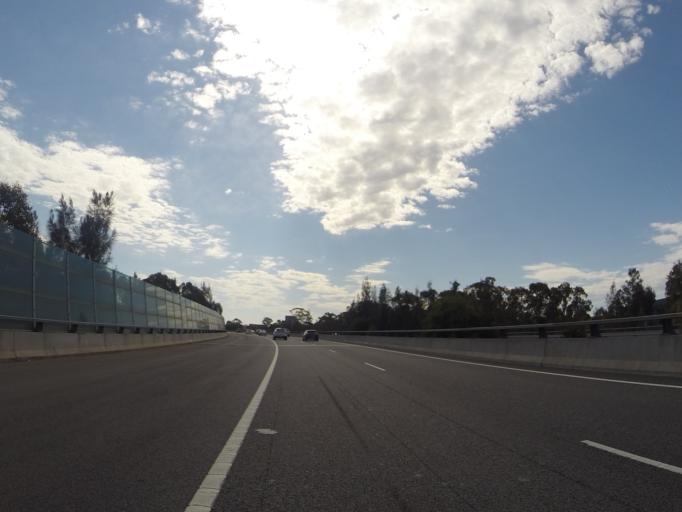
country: AU
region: New South Wales
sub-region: Liverpool
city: Miller
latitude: -33.9408
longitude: 150.8789
